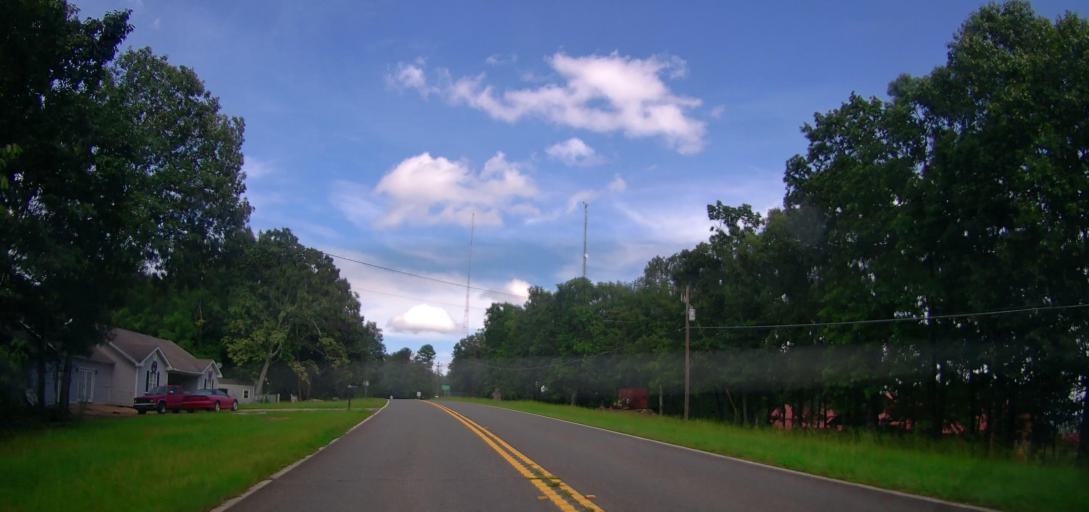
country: US
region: Georgia
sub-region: Meriwether County
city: Manchester
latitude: 32.8441
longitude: -84.6261
